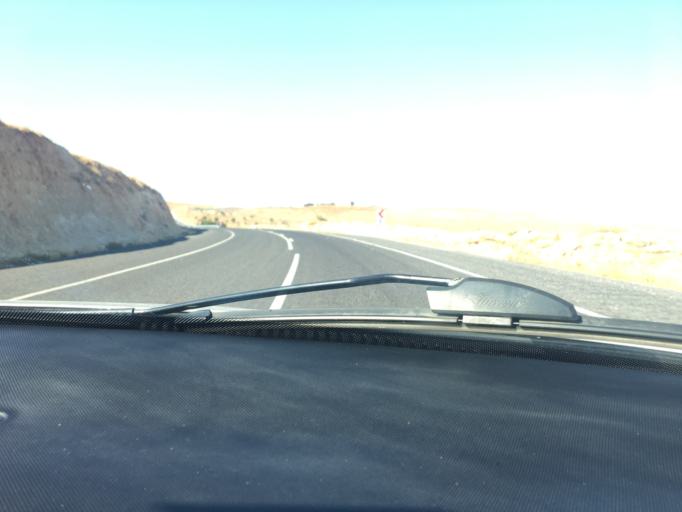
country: TR
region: Sanliurfa
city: Bogurtlen
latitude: 37.1670
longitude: 37.9821
